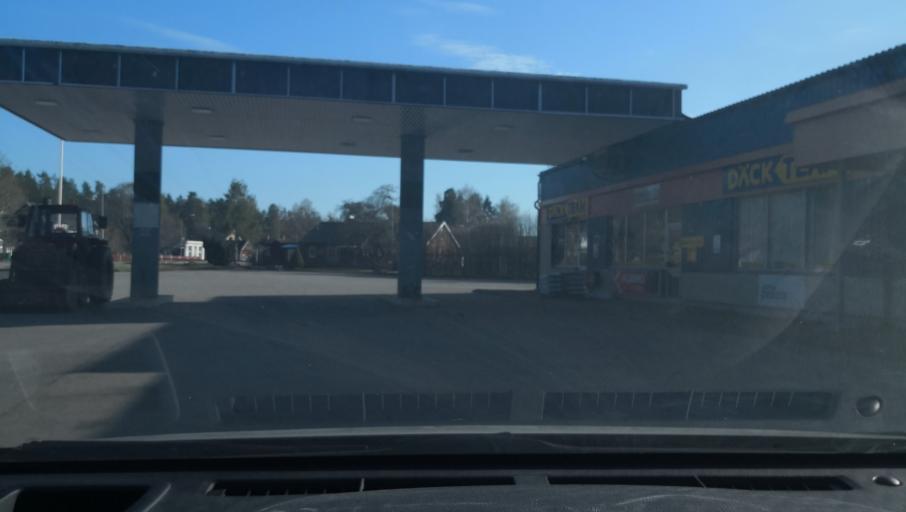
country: SE
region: Uppsala
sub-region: Heby Kommun
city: Tarnsjo
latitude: 60.1631
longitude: 16.9377
